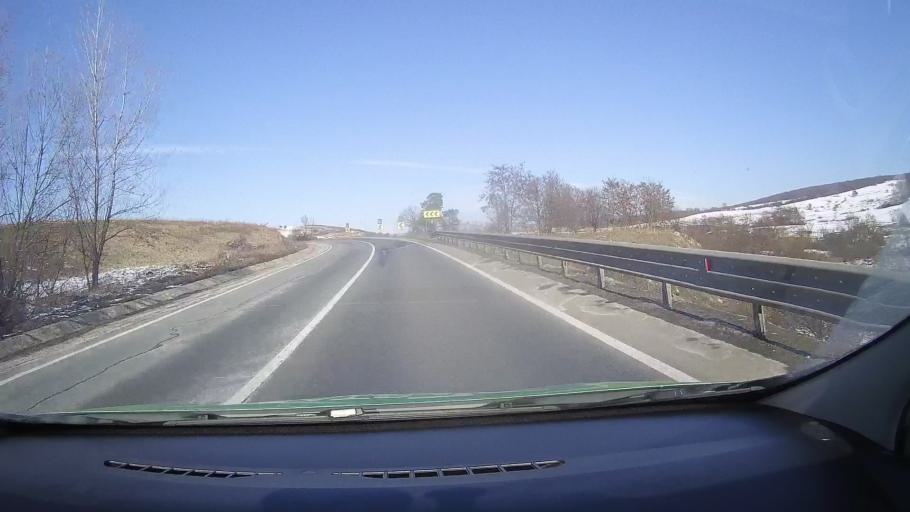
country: RO
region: Brasov
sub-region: Oras Rupea
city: Fiser
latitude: 46.0585
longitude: 25.1787
